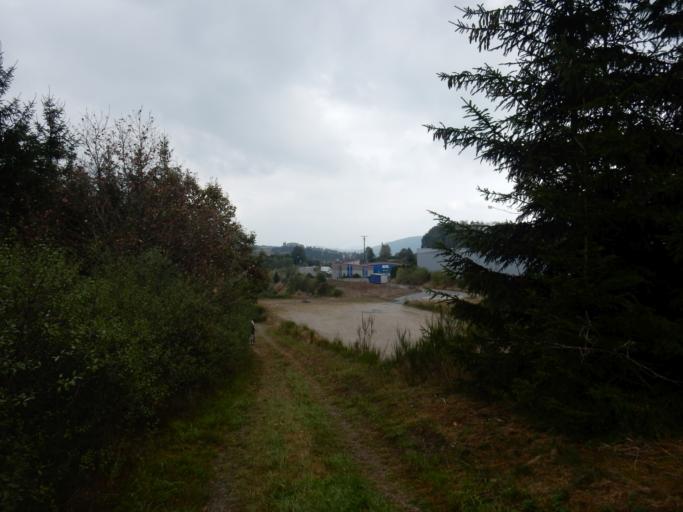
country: LU
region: Diekirch
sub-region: Canton de Wiltz
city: Winseler
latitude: 49.9608
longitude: 5.9023
